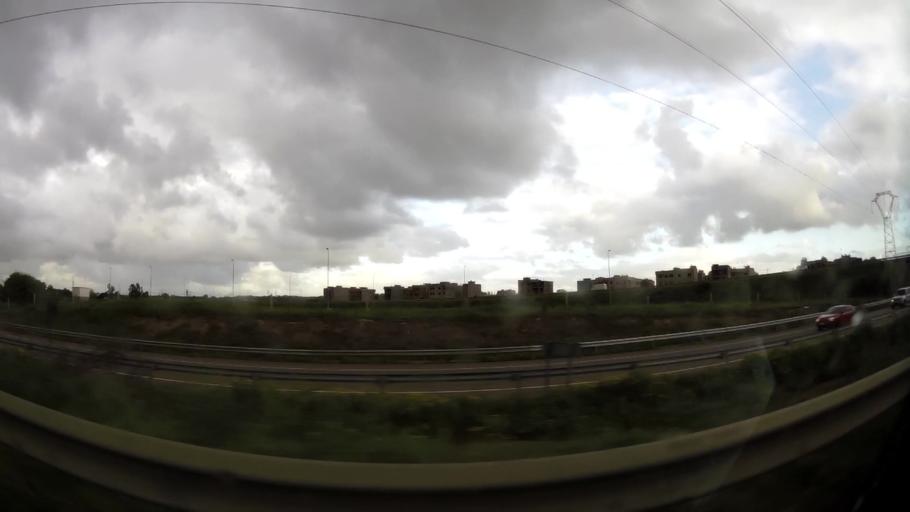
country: MA
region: Grand Casablanca
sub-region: Mohammedia
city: Mohammedia
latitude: 33.6460
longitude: -7.4211
